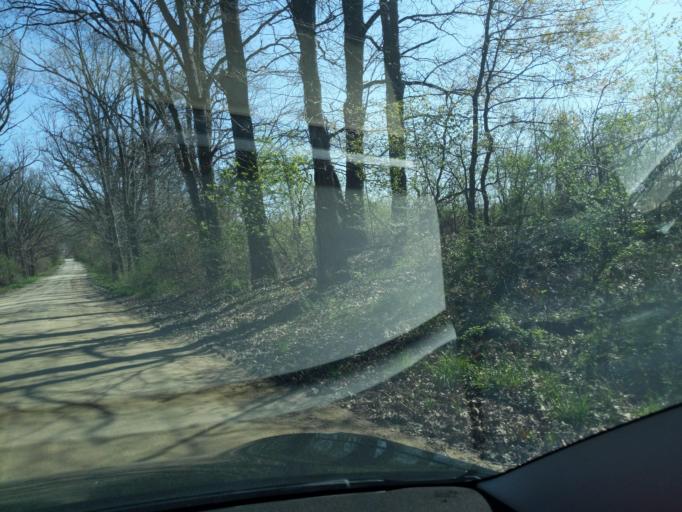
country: US
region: Michigan
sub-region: Ingham County
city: Stockbridge
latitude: 42.4297
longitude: -84.0825
